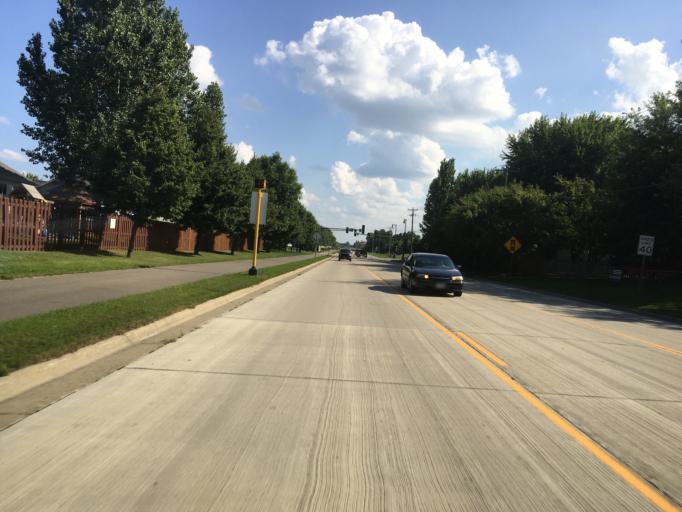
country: US
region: Minnesota
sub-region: Stearns County
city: Sartell
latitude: 45.6240
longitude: -94.2273
